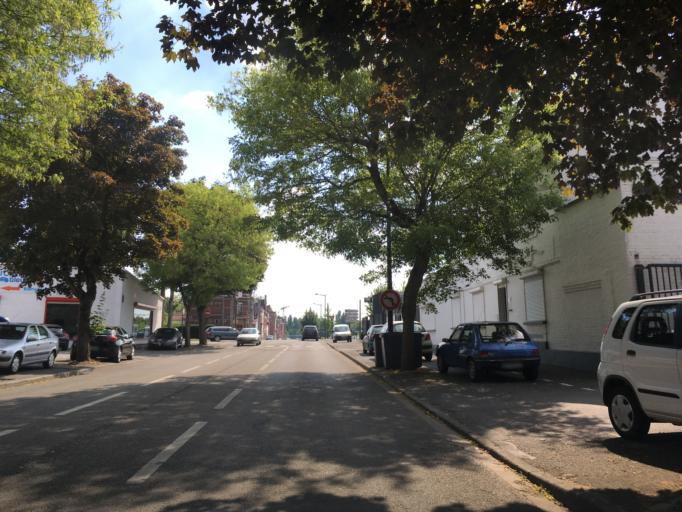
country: FR
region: Nord-Pas-de-Calais
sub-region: Departement du Nord
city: Valenciennes
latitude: 50.3503
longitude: 3.5215
